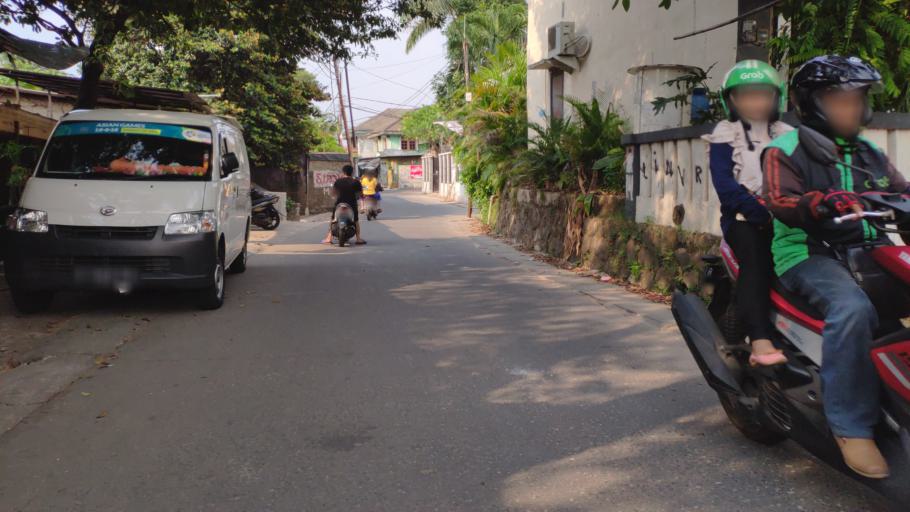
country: ID
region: West Java
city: Pamulang
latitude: -6.3202
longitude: 106.7937
